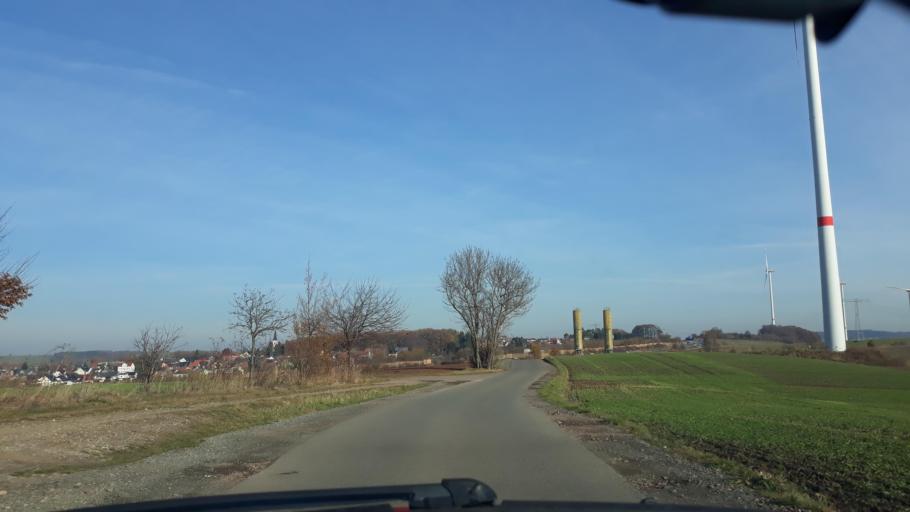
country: DE
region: Saxony
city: Reinsdorf
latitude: 50.6729
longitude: 12.5572
